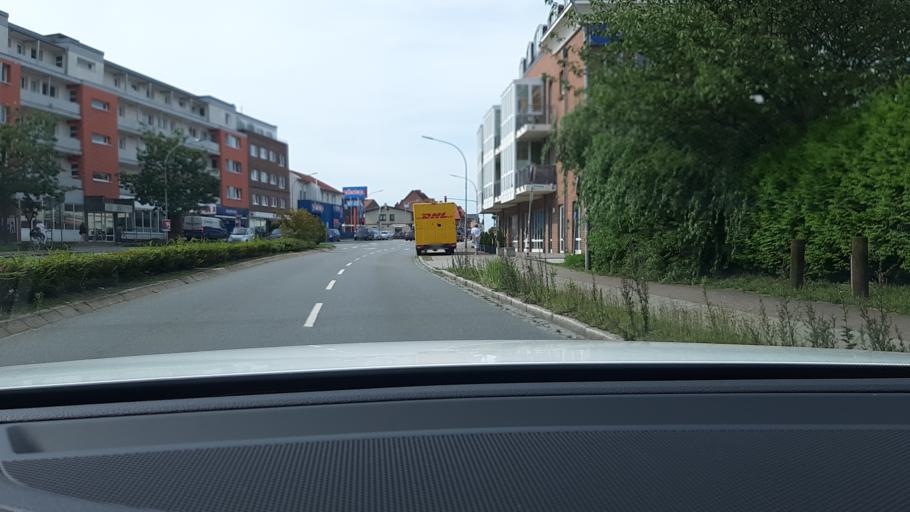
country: DE
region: Schleswig-Holstein
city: Stockelsdorf
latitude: 53.8863
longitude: 10.6516
